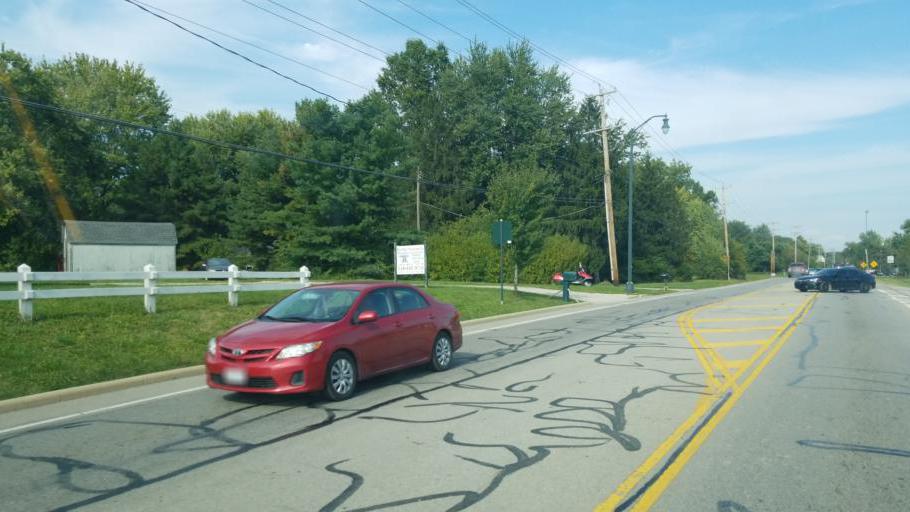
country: US
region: Ohio
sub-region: Franklin County
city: New Albany
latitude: 40.0929
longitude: -82.7880
